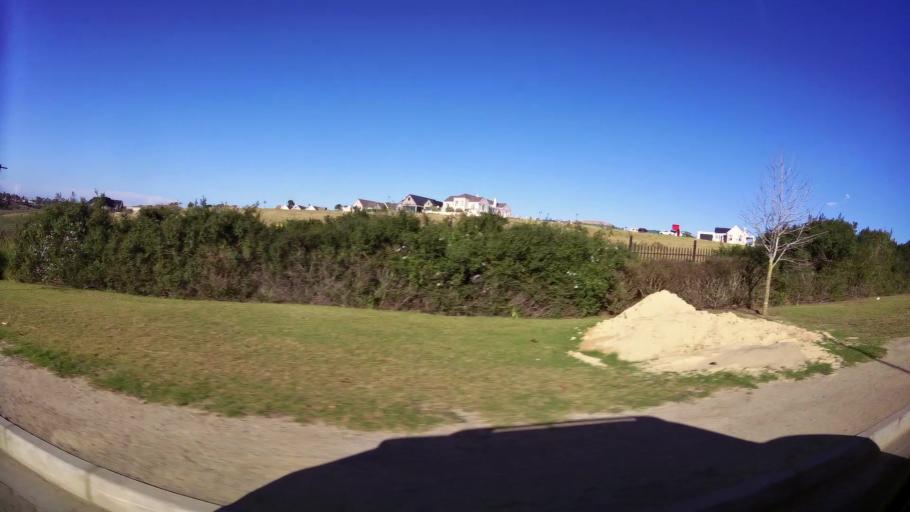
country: ZA
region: Western Cape
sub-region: Eden District Municipality
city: George
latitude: -33.9659
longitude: 22.4326
